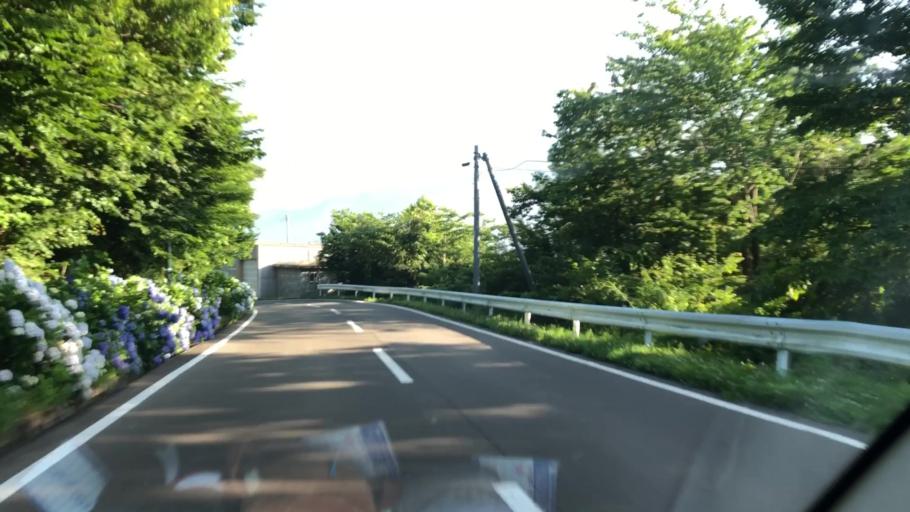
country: JP
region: Miyagi
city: Shiroishi
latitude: 38.0254
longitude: 140.5431
